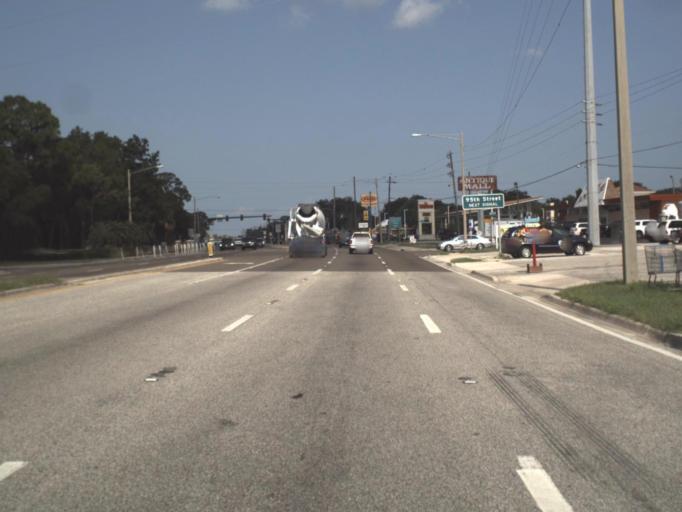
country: US
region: Florida
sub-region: Pinellas County
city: Bay Pines
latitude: 27.8138
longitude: -82.7686
